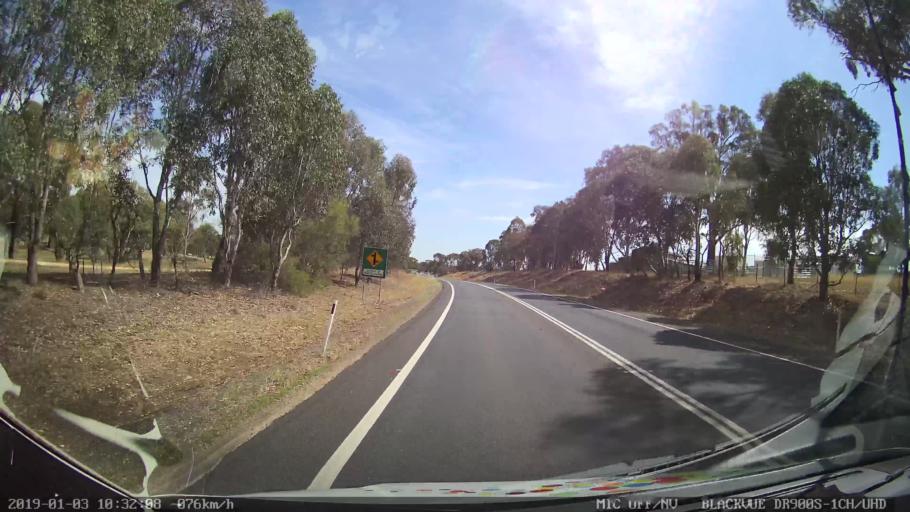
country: AU
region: New South Wales
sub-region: Young
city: Young
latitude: -34.3423
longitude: 148.2827
